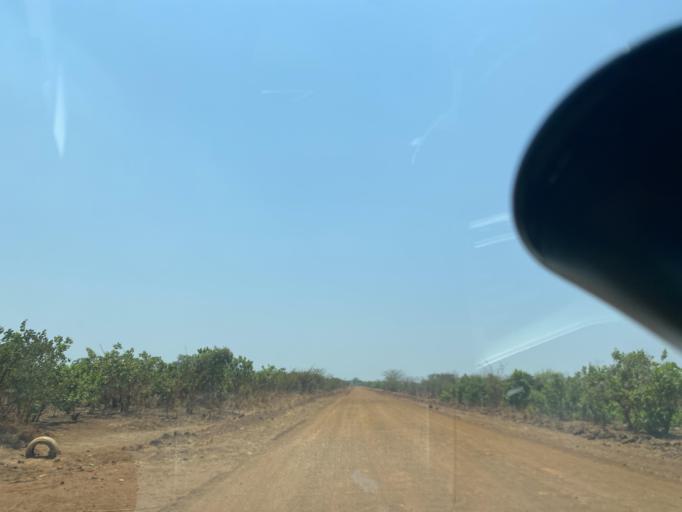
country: ZM
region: Lusaka
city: Lusaka
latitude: -15.4554
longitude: 27.9418
